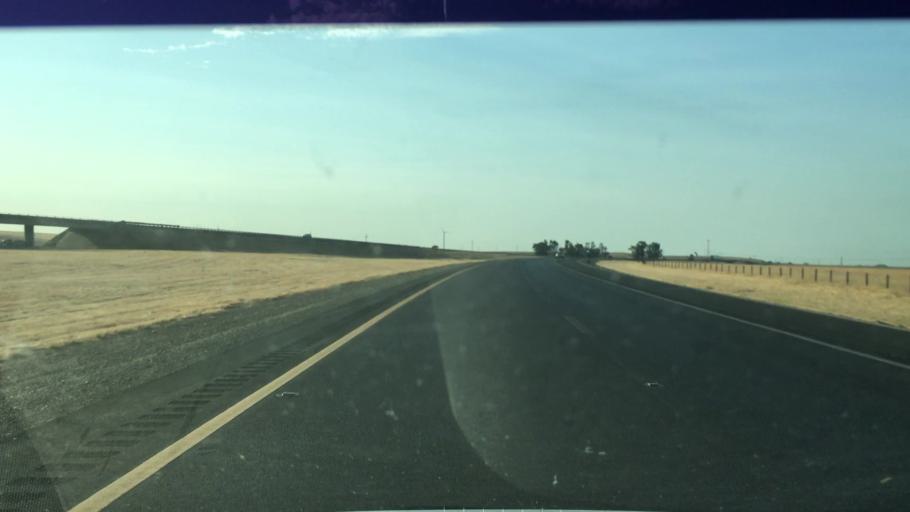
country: US
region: California
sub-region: San Joaquin County
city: Tracy
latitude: 37.5971
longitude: -121.3402
